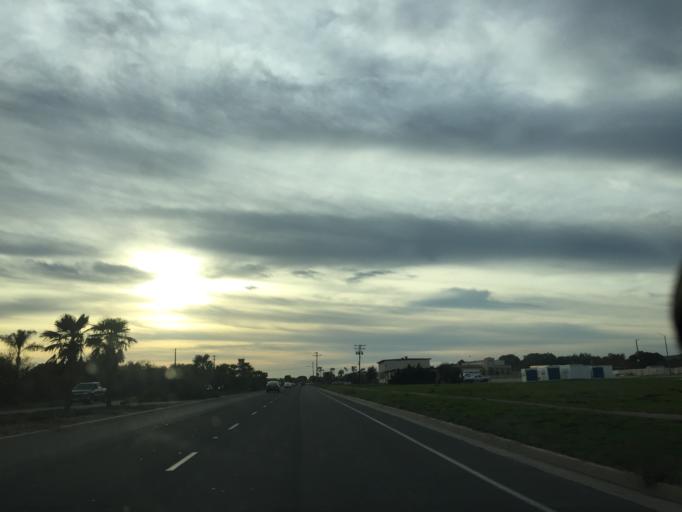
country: US
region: California
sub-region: Santa Barbara County
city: Goleta
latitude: 34.4343
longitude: -119.8358
